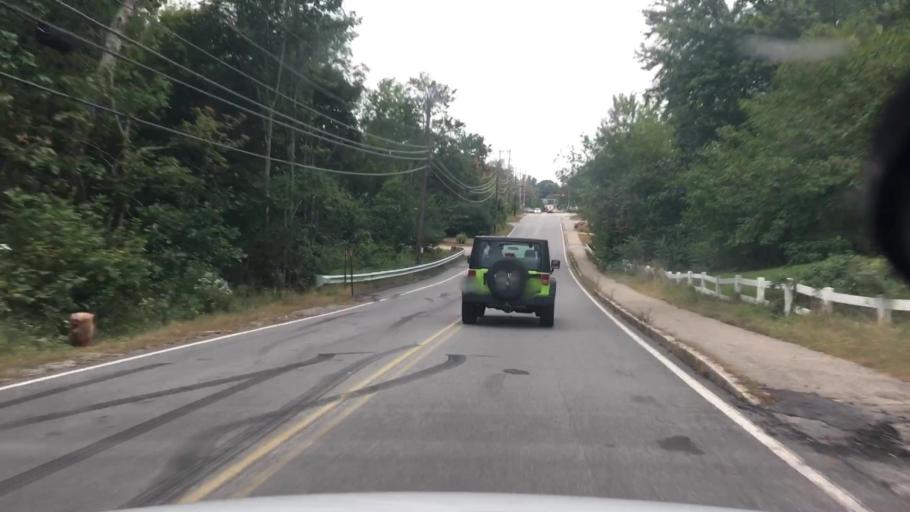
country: US
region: New Hampshire
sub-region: Strafford County
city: Rochester
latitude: 43.2918
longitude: -70.9701
